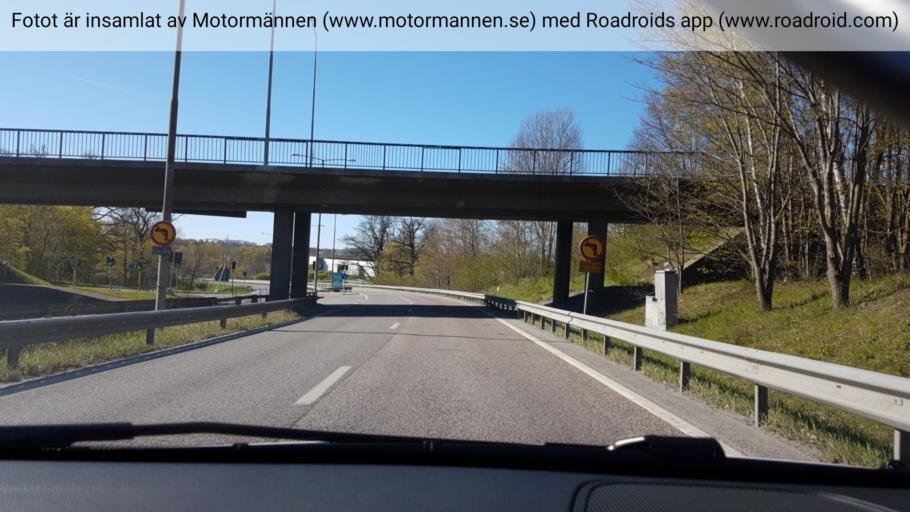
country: SE
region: Stockholm
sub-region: Stockholms Kommun
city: Arsta
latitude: 59.2834
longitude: 18.0195
